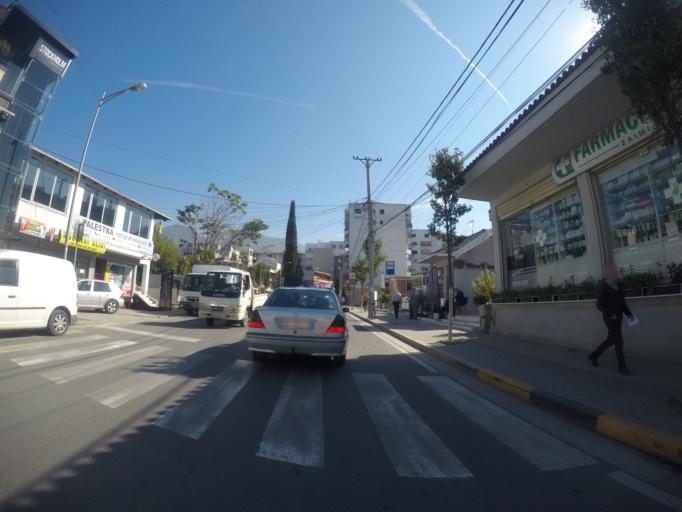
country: AL
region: Tirane
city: Tirana
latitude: 41.3461
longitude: 19.8544
